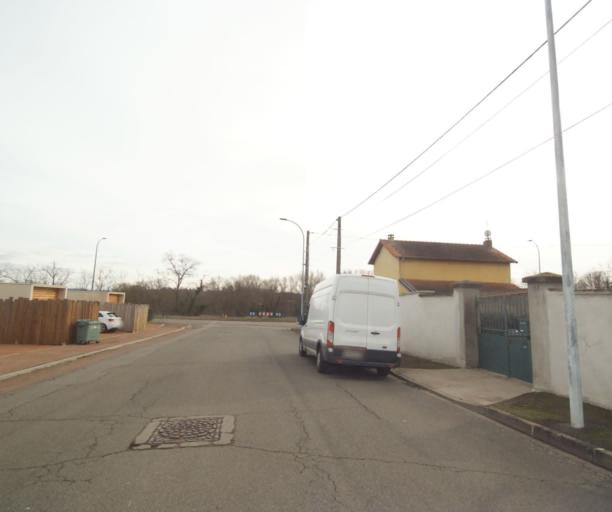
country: FR
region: Rhone-Alpes
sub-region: Departement de la Loire
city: Roanne
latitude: 46.0190
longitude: 4.0575
